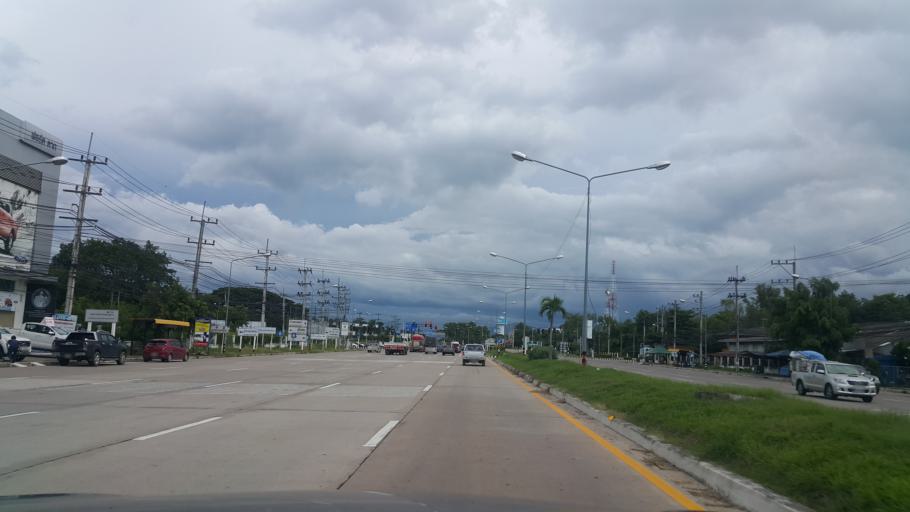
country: TH
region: Tak
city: Tak
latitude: 16.8869
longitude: 99.1277
